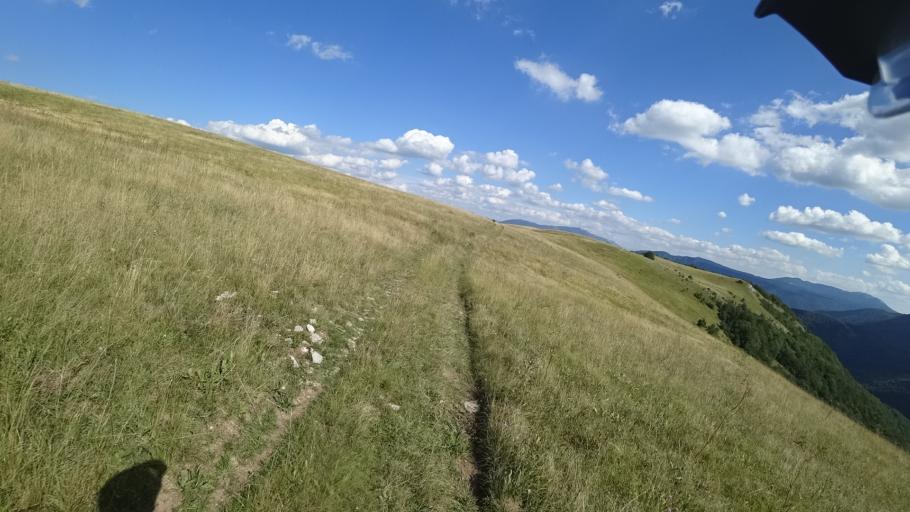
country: HR
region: Zadarska
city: Gracac
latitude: 44.3707
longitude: 16.0673
